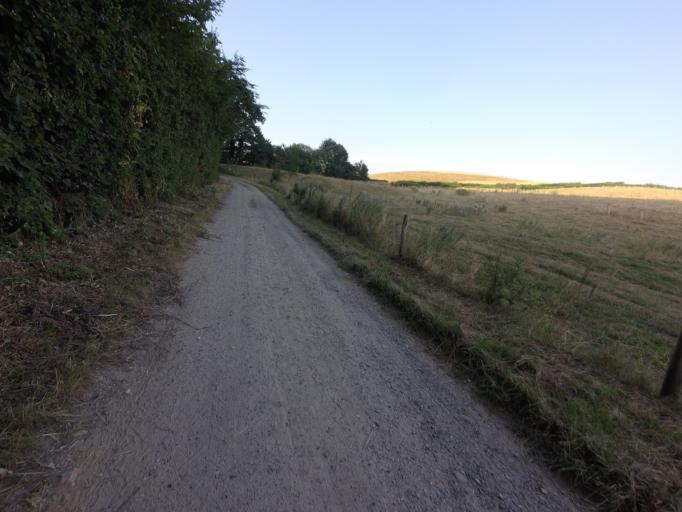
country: NL
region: Limburg
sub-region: Eijsden-Margraten
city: Margraten
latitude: 50.7835
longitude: 5.8800
